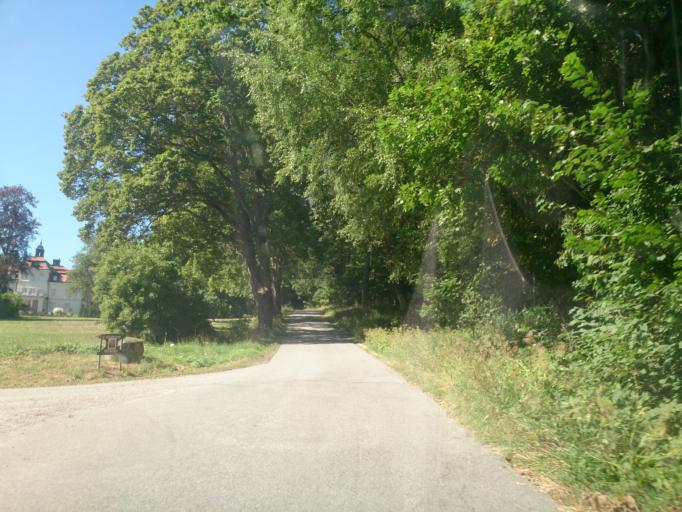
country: SE
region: OEstergoetland
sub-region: Norrkopings Kommun
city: Jursla
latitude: 58.6740
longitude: 16.1294
